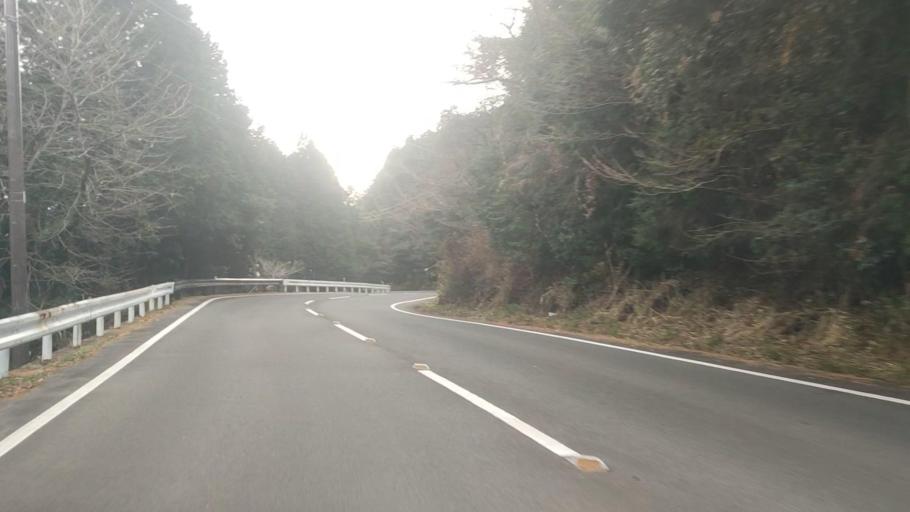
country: JP
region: Nagasaki
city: Shimabara
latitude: 32.7201
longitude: 130.2471
